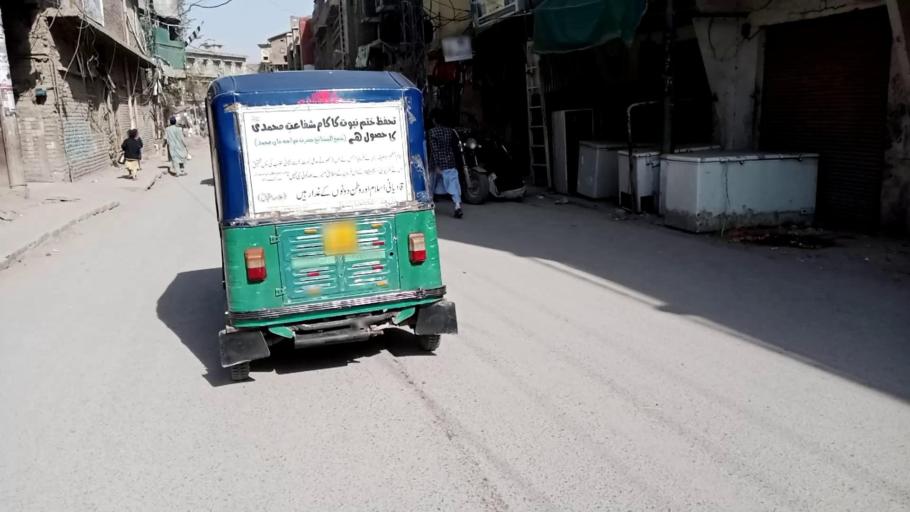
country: PK
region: Khyber Pakhtunkhwa
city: Peshawar
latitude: 34.0011
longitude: 71.5783
